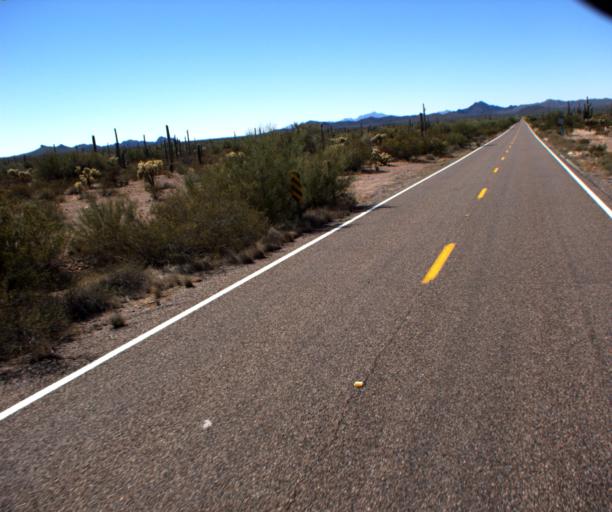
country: MX
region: Sonora
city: Sonoyta
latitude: 32.0562
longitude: -112.7890
